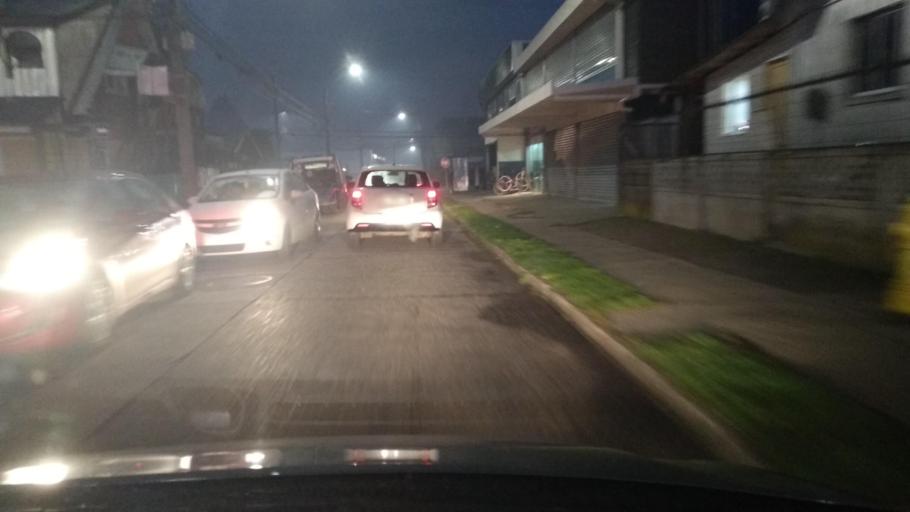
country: CL
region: Los Rios
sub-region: Provincia de Valdivia
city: Valdivia
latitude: -39.8152
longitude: -73.2564
